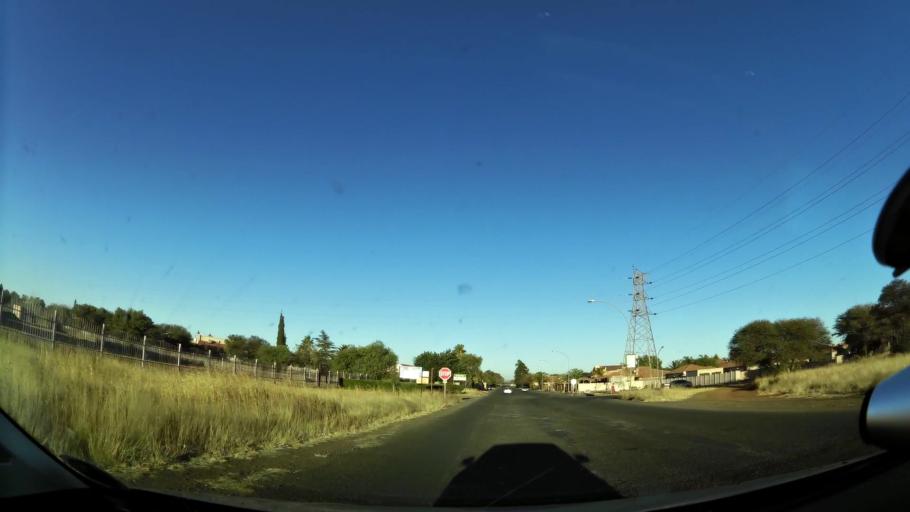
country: ZA
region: Northern Cape
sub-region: Frances Baard District Municipality
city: Kimberley
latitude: -28.7619
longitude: 24.7442
